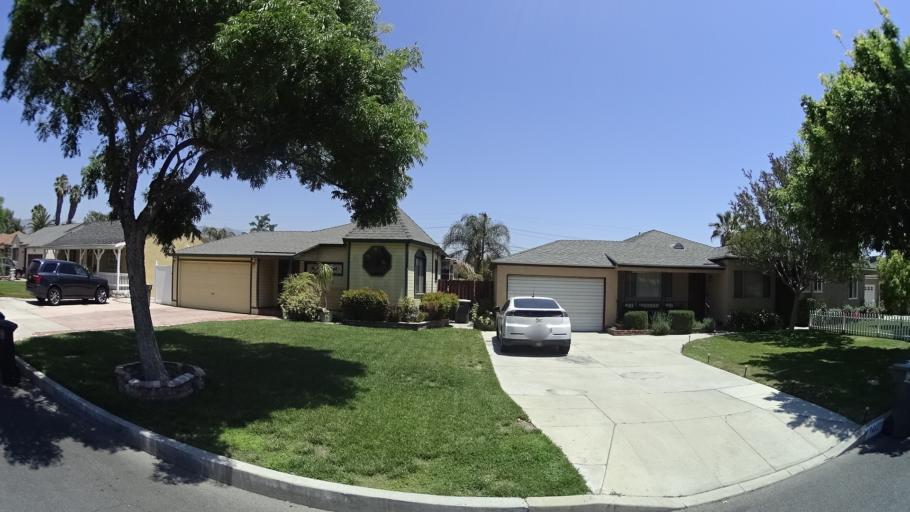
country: US
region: California
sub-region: Los Angeles County
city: Burbank
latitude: 34.1816
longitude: -118.3395
